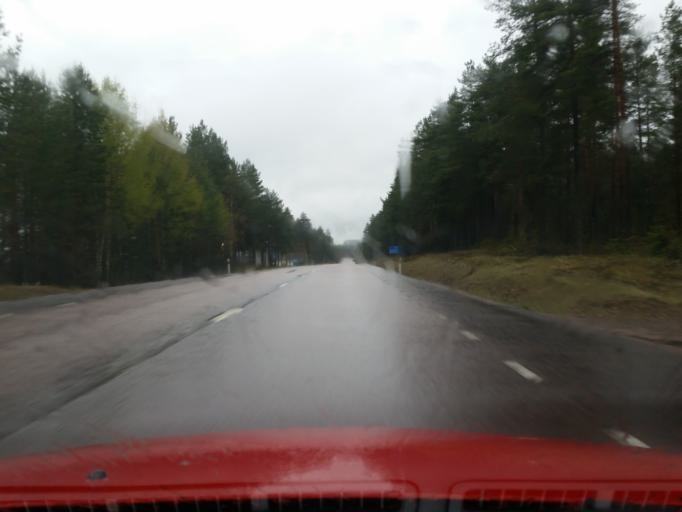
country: SE
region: Dalarna
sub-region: Leksand Municipality
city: Smedby
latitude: 60.6662
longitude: 15.0878
